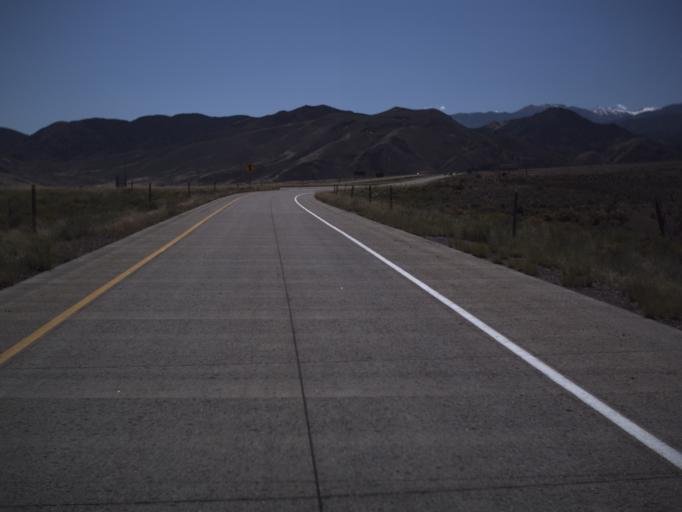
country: US
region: Utah
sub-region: Sevier County
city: Monroe
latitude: 38.6218
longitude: -112.2283
